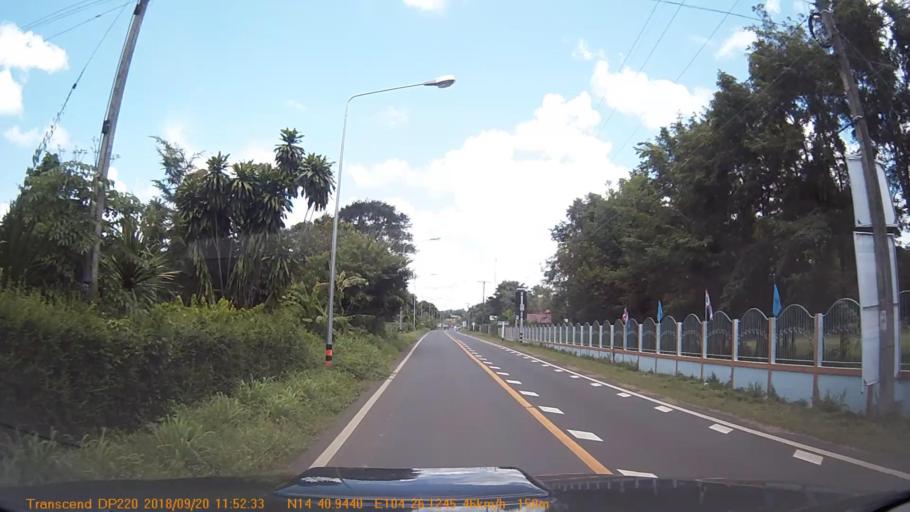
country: TH
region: Sisaket
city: Khun Han
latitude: 14.6828
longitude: 104.4353
